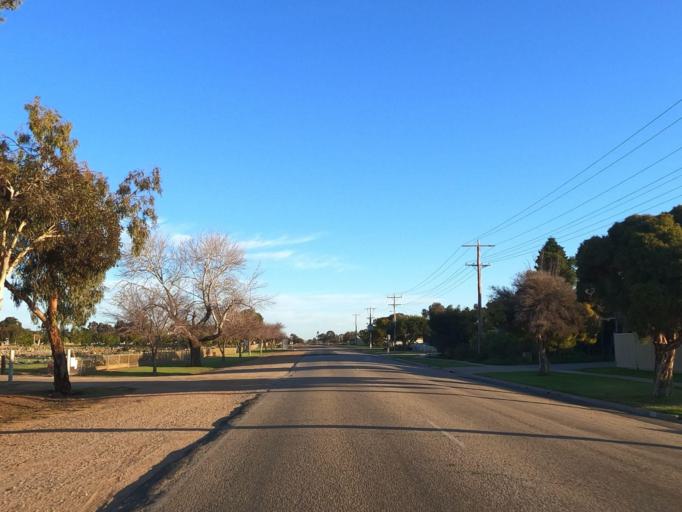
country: AU
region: Victoria
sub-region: Swan Hill
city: Swan Hill
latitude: -35.3524
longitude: 143.5535
